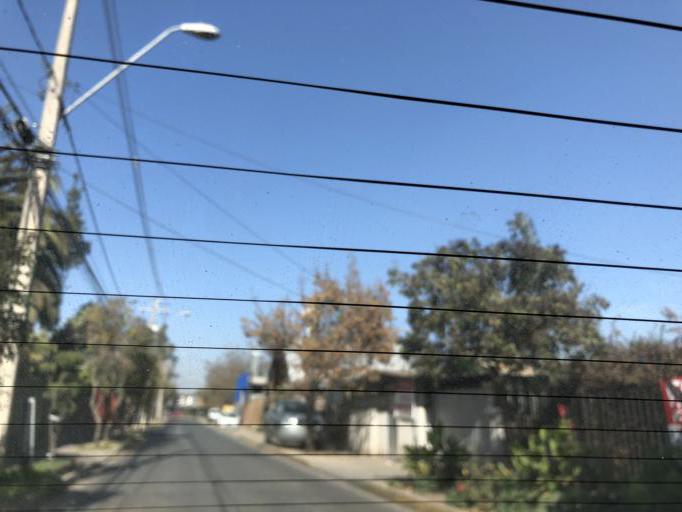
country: CL
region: Santiago Metropolitan
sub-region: Provincia de Cordillera
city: Puente Alto
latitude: -33.6036
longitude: -70.5912
